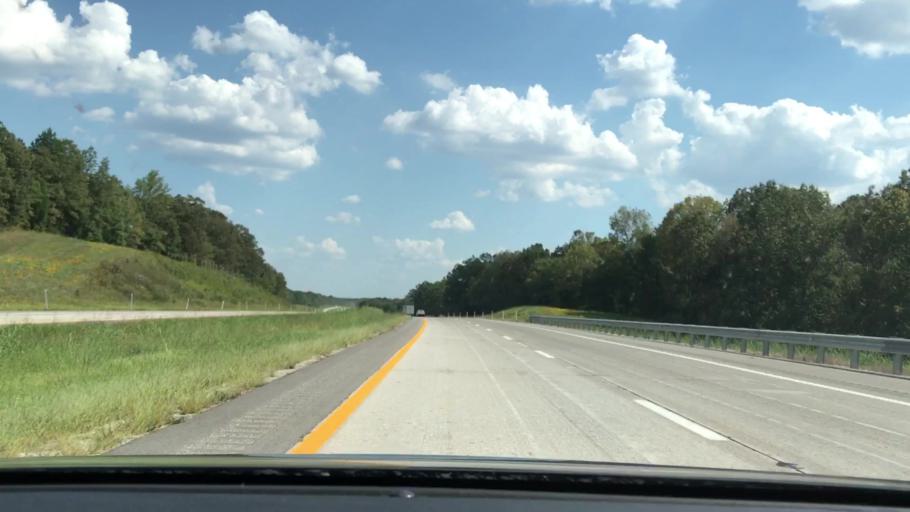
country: US
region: Kentucky
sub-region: Ohio County
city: Oak Grove
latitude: 37.3500
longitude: -86.7838
